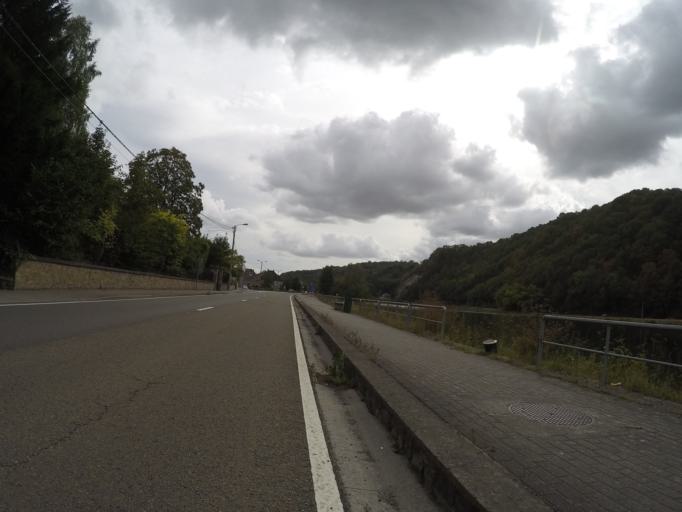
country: BE
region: Wallonia
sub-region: Province de Namur
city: Yvoir
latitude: 50.3328
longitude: 4.8739
